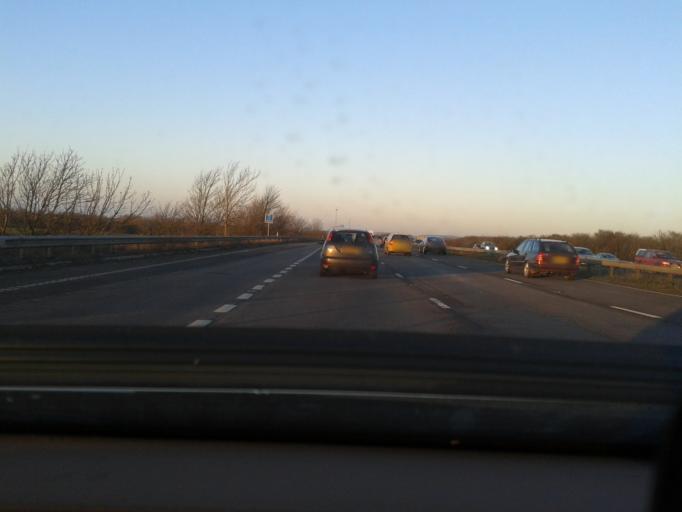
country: GB
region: England
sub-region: North Somerset
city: St. Georges
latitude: 51.3654
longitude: -2.8913
